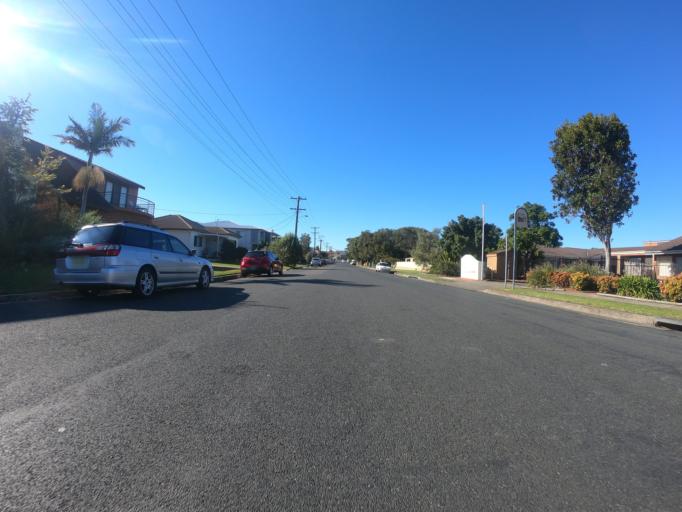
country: AU
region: New South Wales
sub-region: Wollongong
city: Corrimal
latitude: -34.3857
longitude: 150.9089
